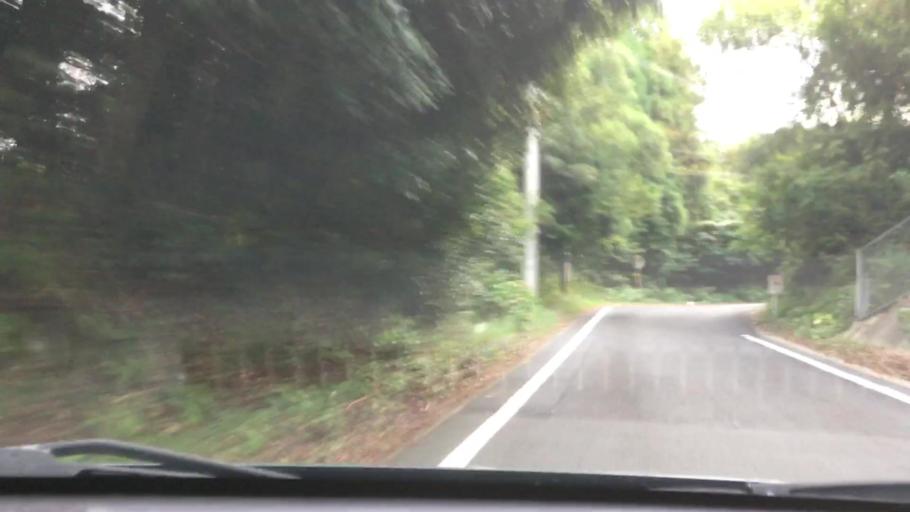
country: JP
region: Nagasaki
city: Sasebo
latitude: 32.9908
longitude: 129.7268
